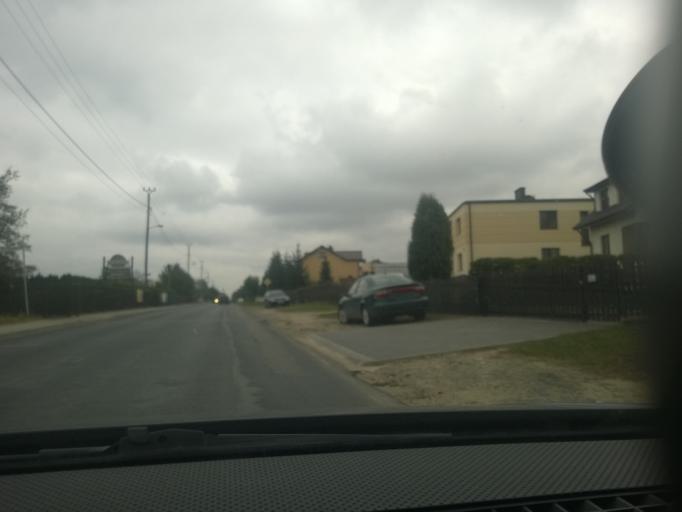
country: PL
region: Greater Poland Voivodeship
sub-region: Powiat kaliski
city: Opatowek
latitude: 51.7244
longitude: 18.1536
